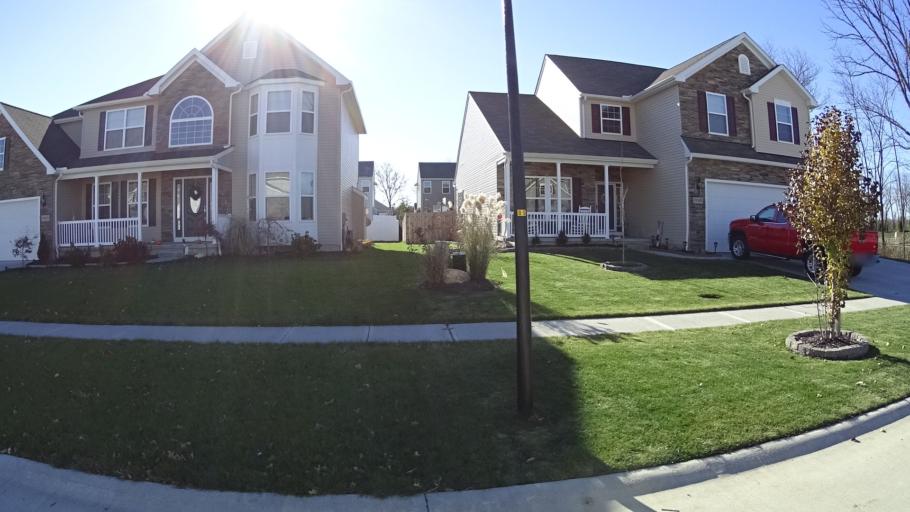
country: US
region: Ohio
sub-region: Lorain County
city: Avon
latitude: 41.4366
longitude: -82.0659
